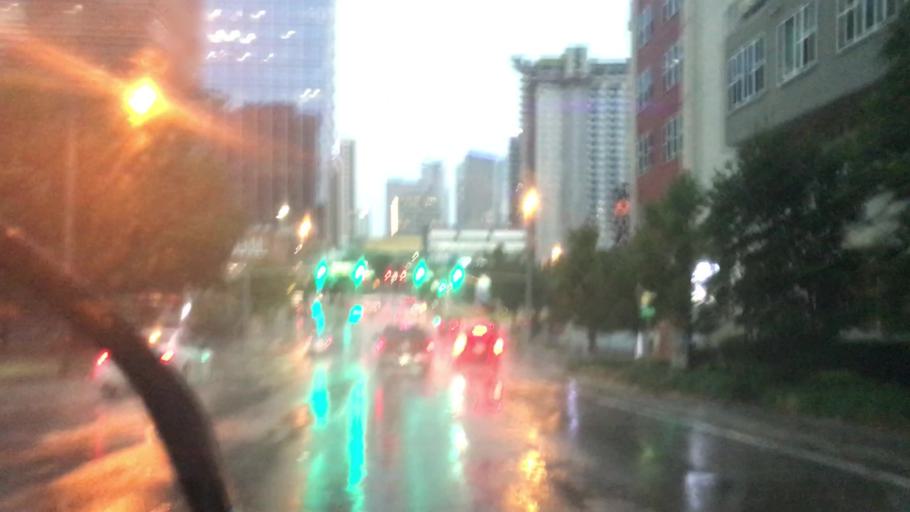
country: US
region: Texas
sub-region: Dallas County
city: Dallas
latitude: 32.7927
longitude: -96.8080
